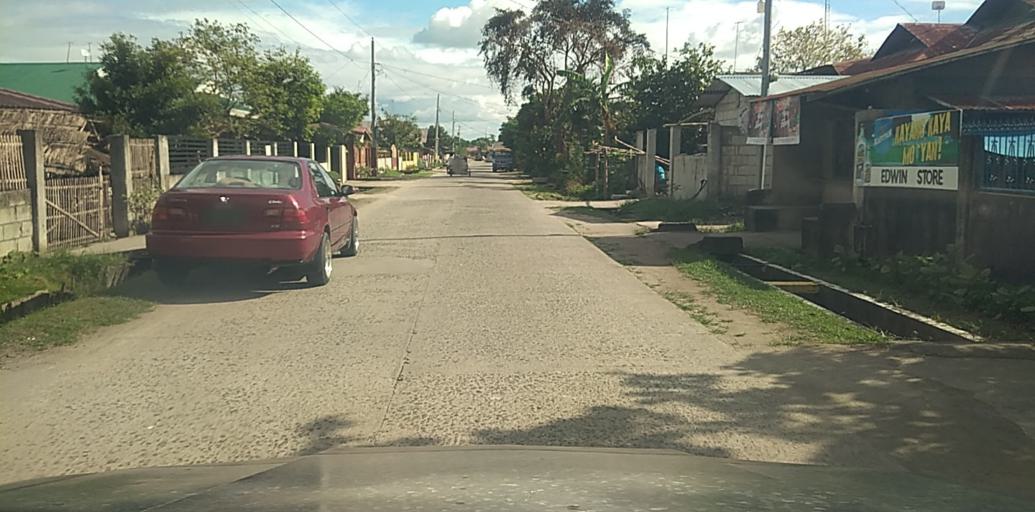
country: PH
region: Central Luzon
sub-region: Province of Pampanga
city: Panlinlang
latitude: 15.1883
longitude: 120.6923
